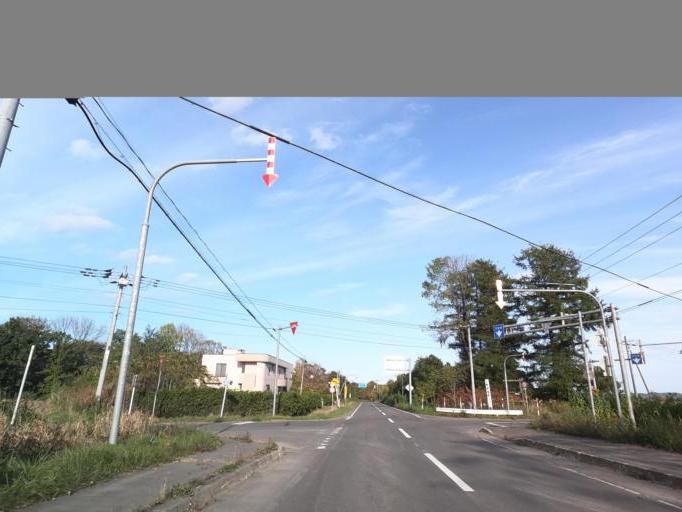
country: JP
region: Hokkaido
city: Obihiro
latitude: 42.5676
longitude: 143.3149
